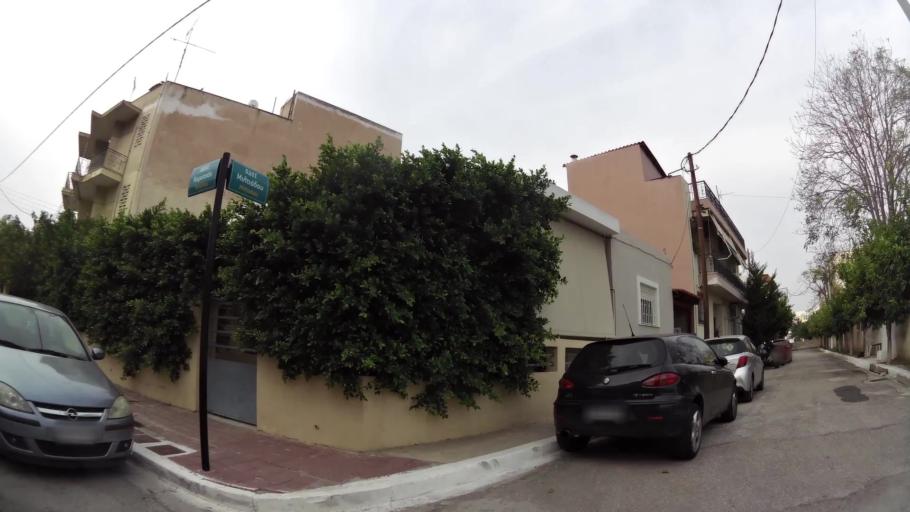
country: GR
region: Attica
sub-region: Nomarchia Athinas
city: Tavros
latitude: 37.9692
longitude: 23.6932
